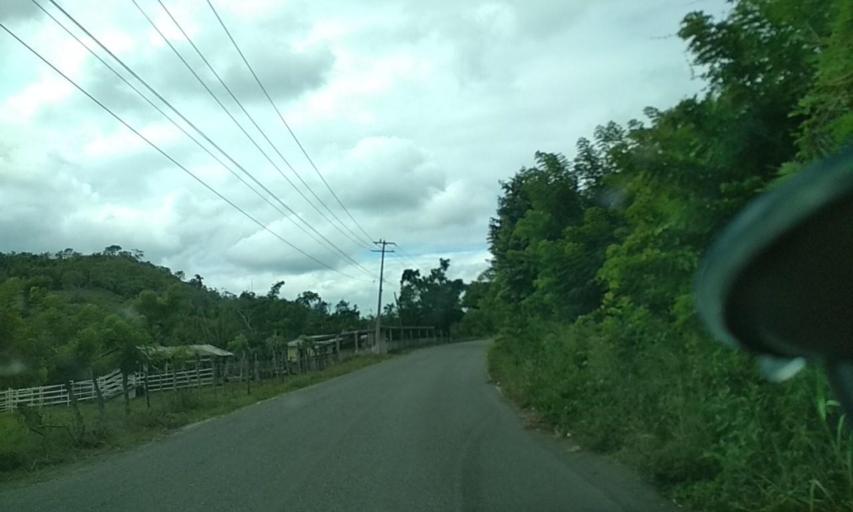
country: MX
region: Veracruz
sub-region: Papantla
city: Residencial Tajin
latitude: 20.6331
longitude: -97.3765
